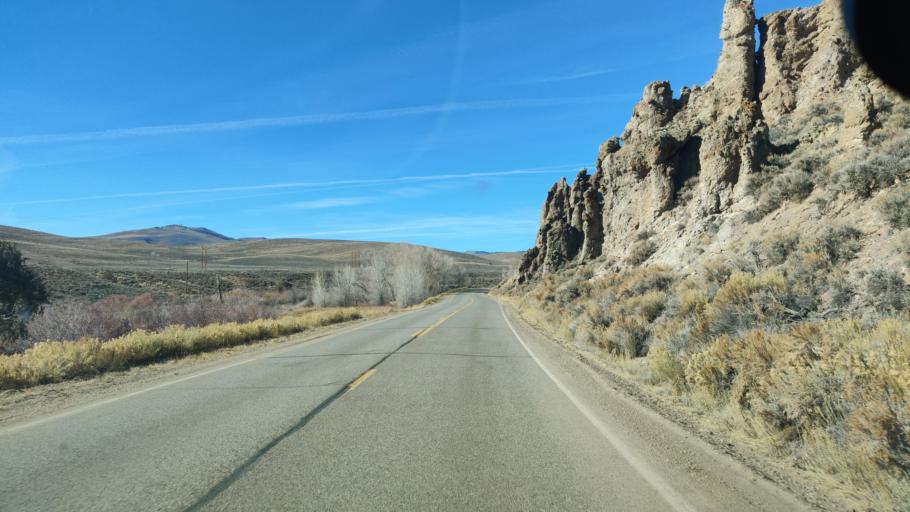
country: US
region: Colorado
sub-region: Gunnison County
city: Gunnison
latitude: 38.5591
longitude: -106.9540
